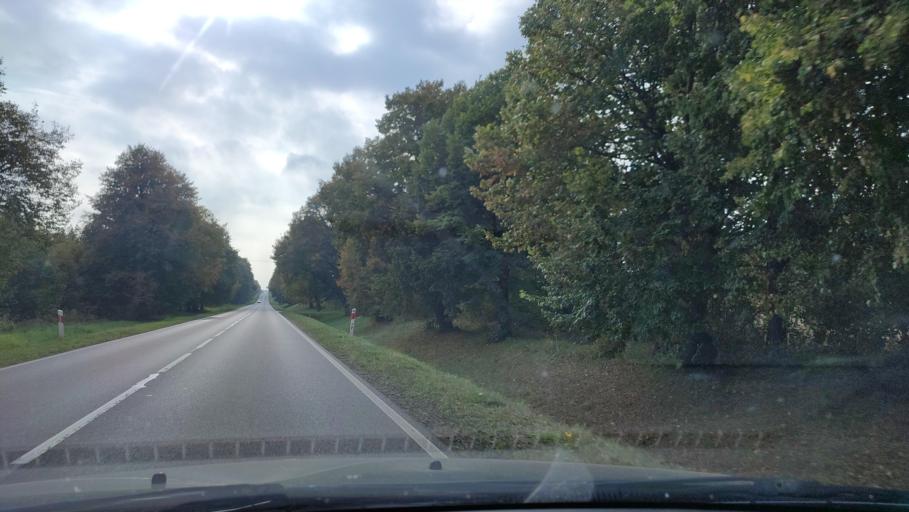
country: PL
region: Warmian-Masurian Voivodeship
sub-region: Powiat nidzicki
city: Kozlowo
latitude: 53.3446
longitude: 20.3471
